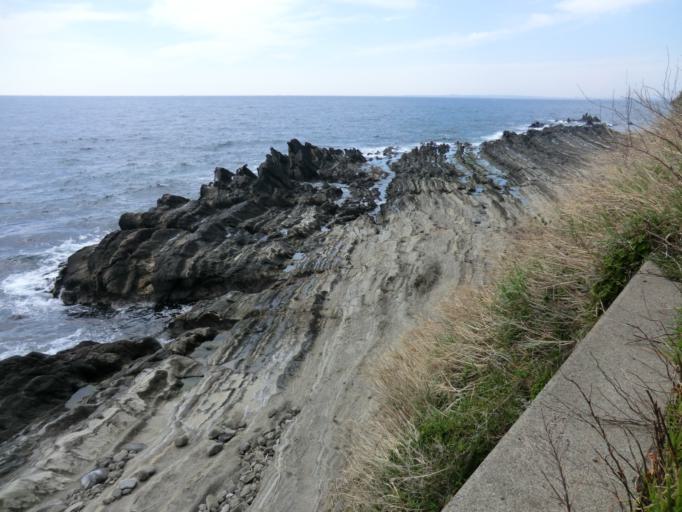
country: JP
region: Chiba
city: Futtsu
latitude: 35.1542
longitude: 139.8201
